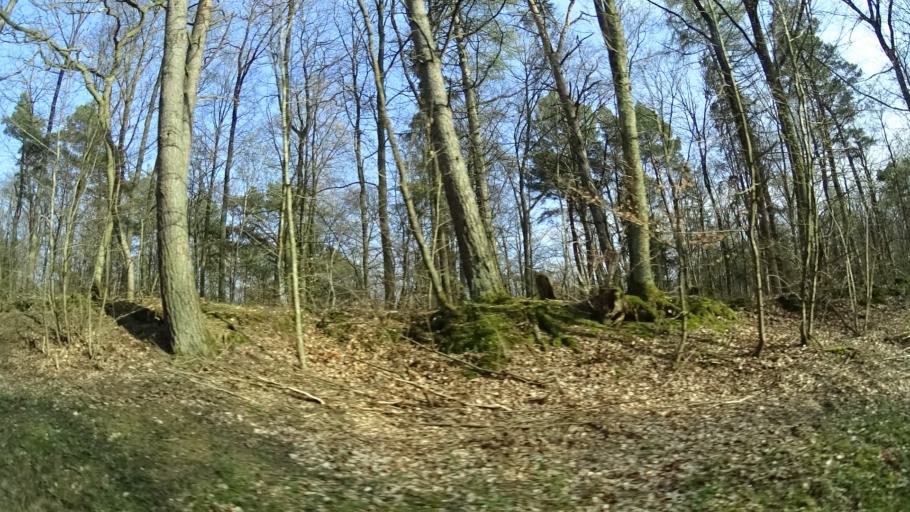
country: DE
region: Rheinland-Pfalz
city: Braunweiler
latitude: 49.8499
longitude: 7.7451
